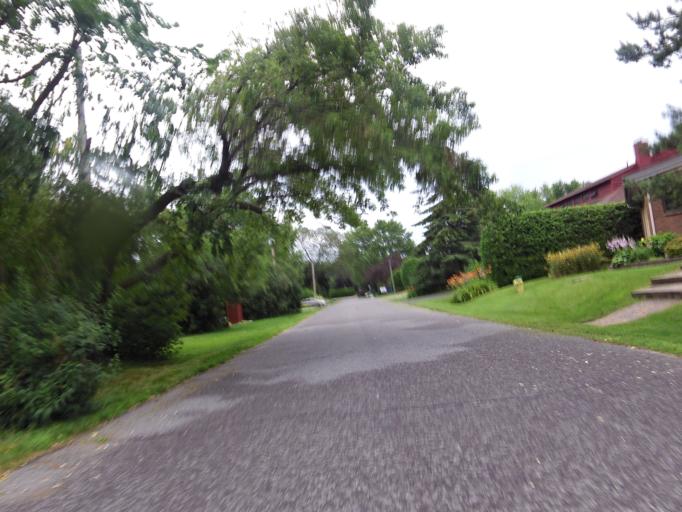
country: CA
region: Ontario
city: Bells Corners
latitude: 45.3555
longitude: -75.8491
